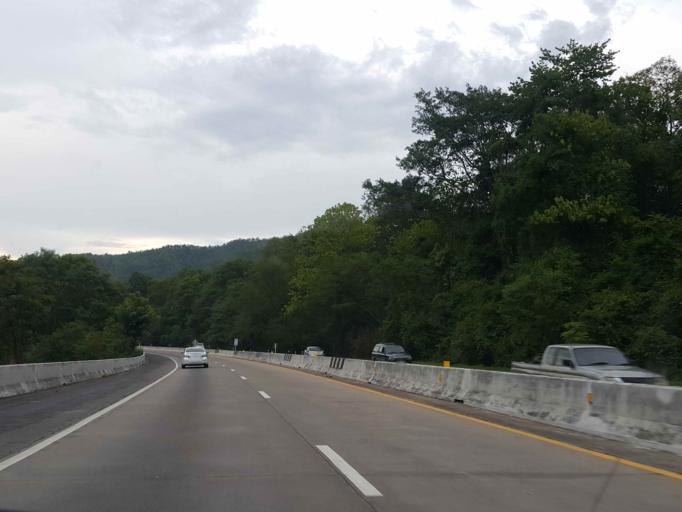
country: TH
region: Lampang
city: Hang Chat
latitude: 18.3703
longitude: 99.2360
